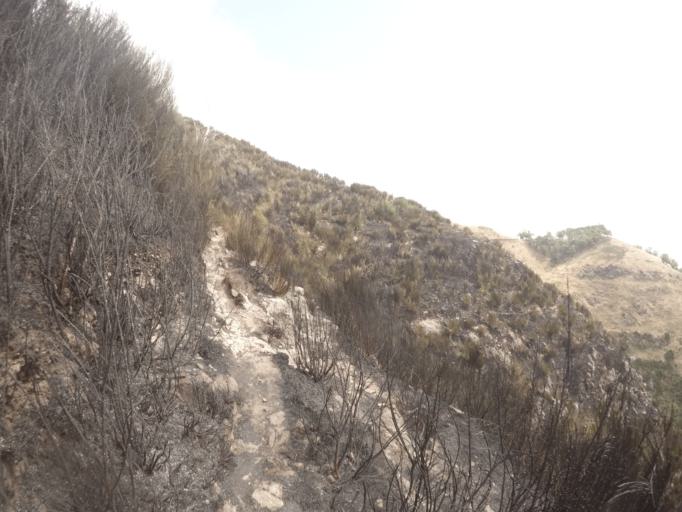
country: PT
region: Madeira
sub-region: Camara de Lobos
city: Curral das Freiras
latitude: 32.7102
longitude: -17.0030
